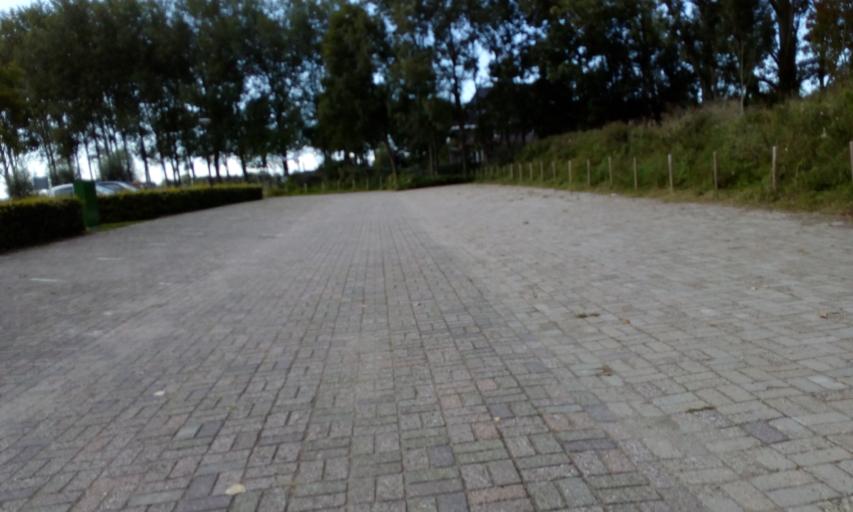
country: NL
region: South Holland
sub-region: Gemeente Leiden
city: Leiden
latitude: 52.1137
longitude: 4.4978
